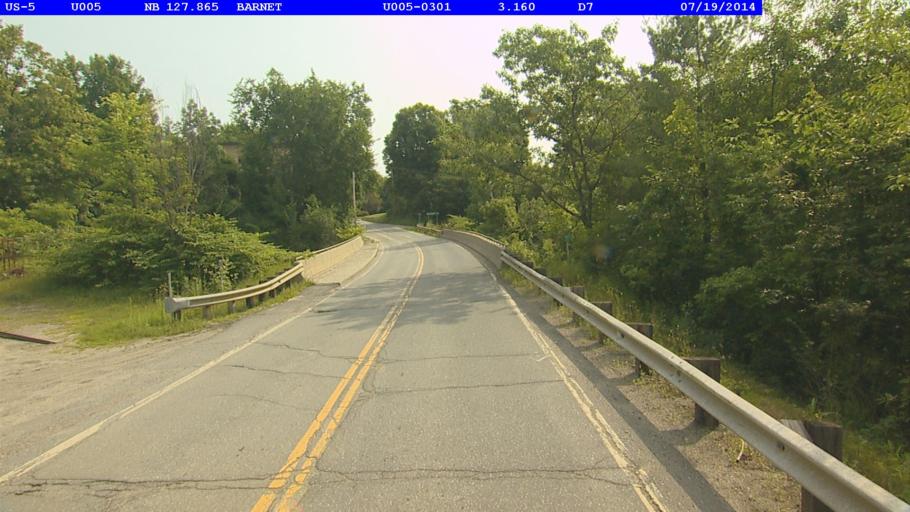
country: US
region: Vermont
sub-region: Caledonia County
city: Saint Johnsbury
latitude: 44.2958
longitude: -72.0503
